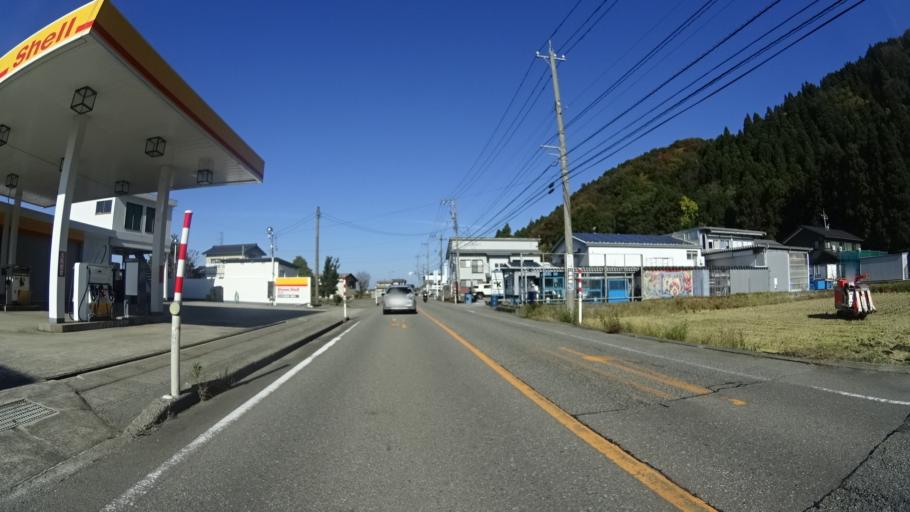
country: JP
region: Ishikawa
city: Tsurugi-asahimachi
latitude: 36.4665
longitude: 136.6190
